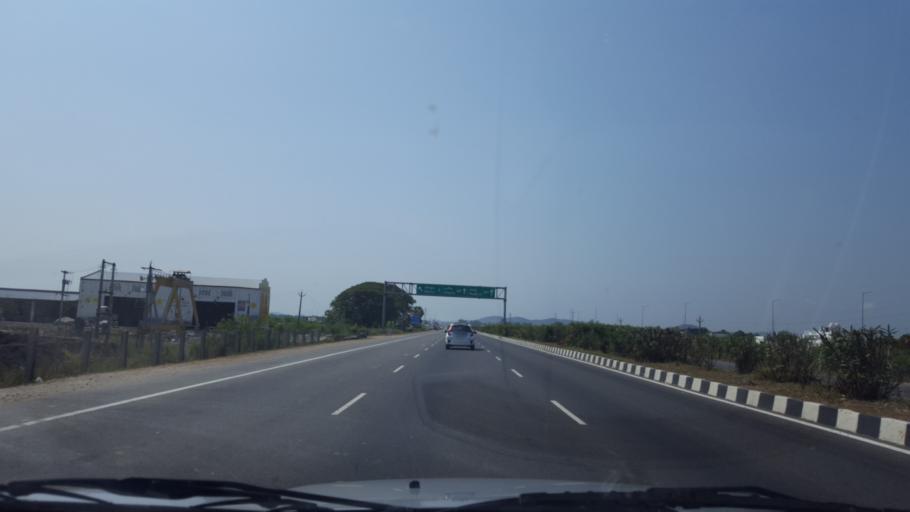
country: IN
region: Andhra Pradesh
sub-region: Guntur
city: Chilakalurupet
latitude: 16.0119
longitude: 80.1181
